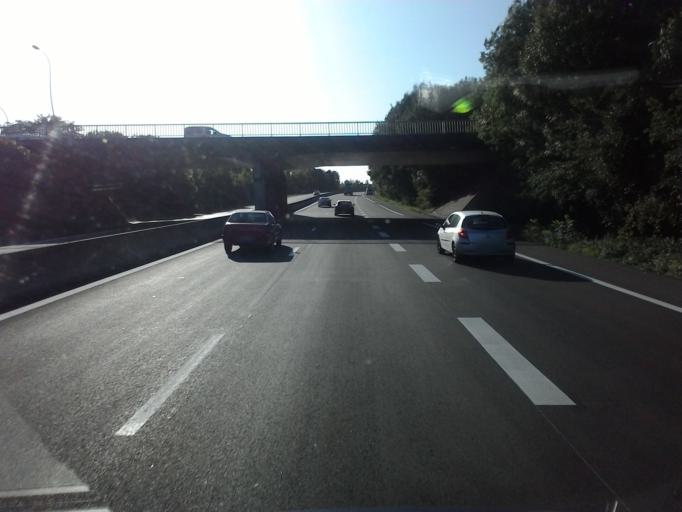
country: FR
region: Champagne-Ardenne
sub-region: Departement de l'Aube
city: Creney-pres-Troyes
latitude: 48.3273
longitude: 4.1164
